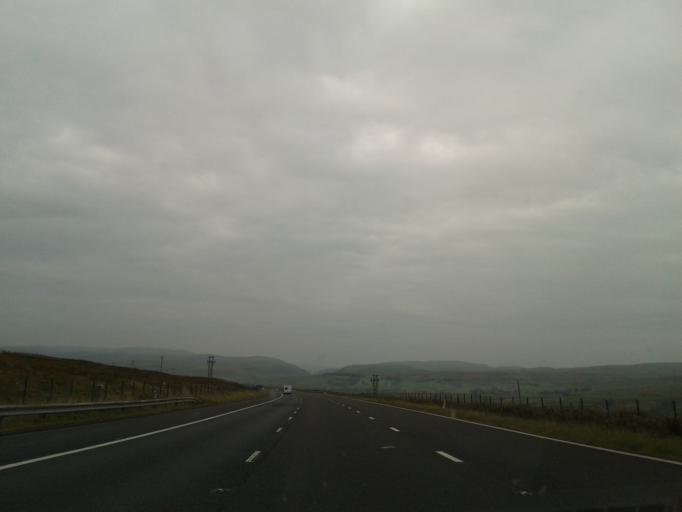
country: GB
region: England
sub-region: Cumbria
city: Appleby-in-Westmorland
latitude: 54.4750
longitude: -2.6309
